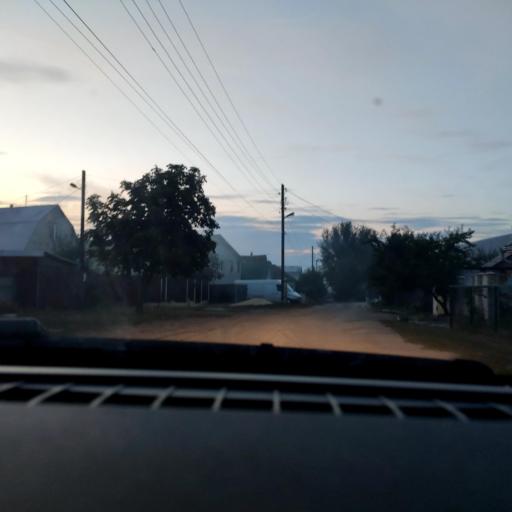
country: RU
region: Voronezj
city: Maslovka
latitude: 51.5570
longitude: 39.2362
